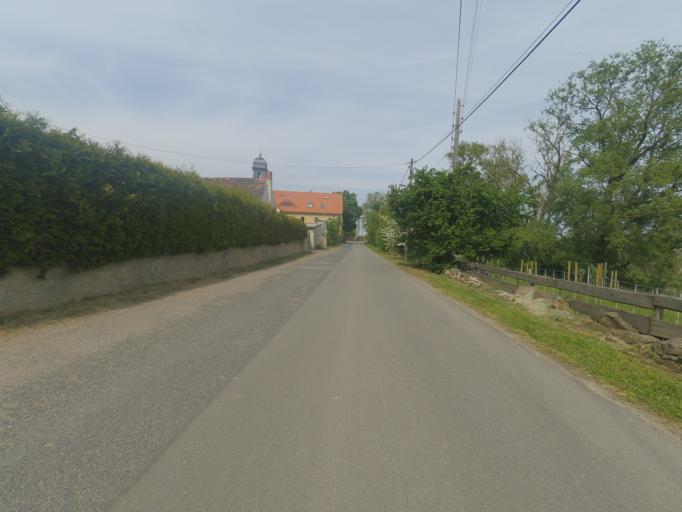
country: DE
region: Saxony
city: Strehla
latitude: 51.3691
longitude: 13.2314
